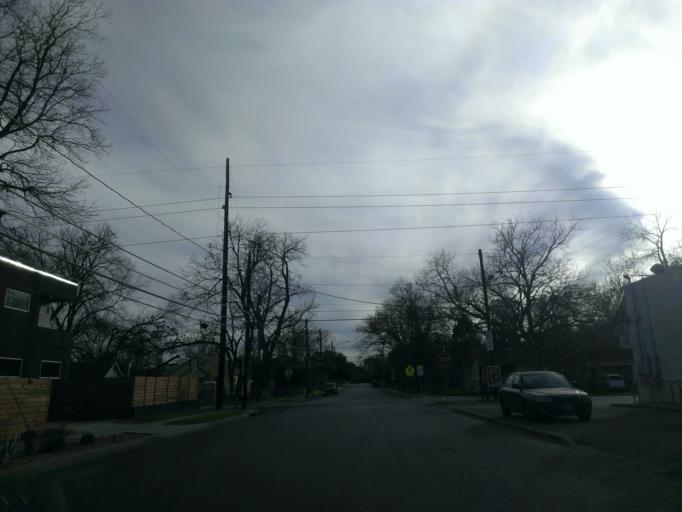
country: US
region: Texas
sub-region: Travis County
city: Austin
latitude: 30.2554
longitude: -97.7301
